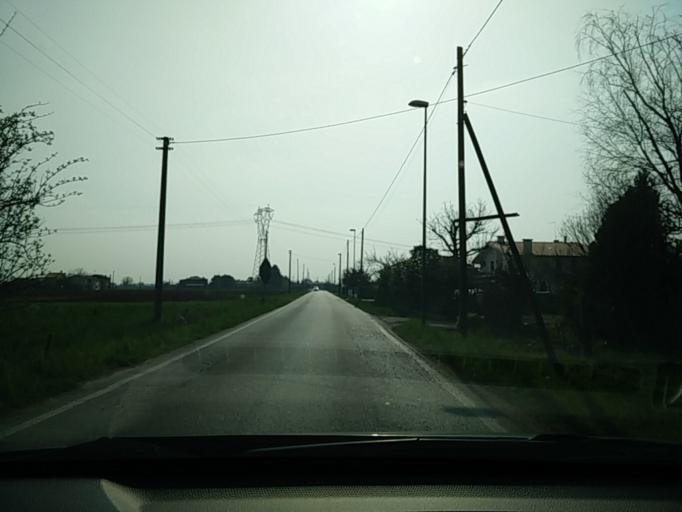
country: IT
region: Veneto
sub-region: Provincia di Treviso
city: Volpago del Montello
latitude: 45.7648
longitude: 12.1291
